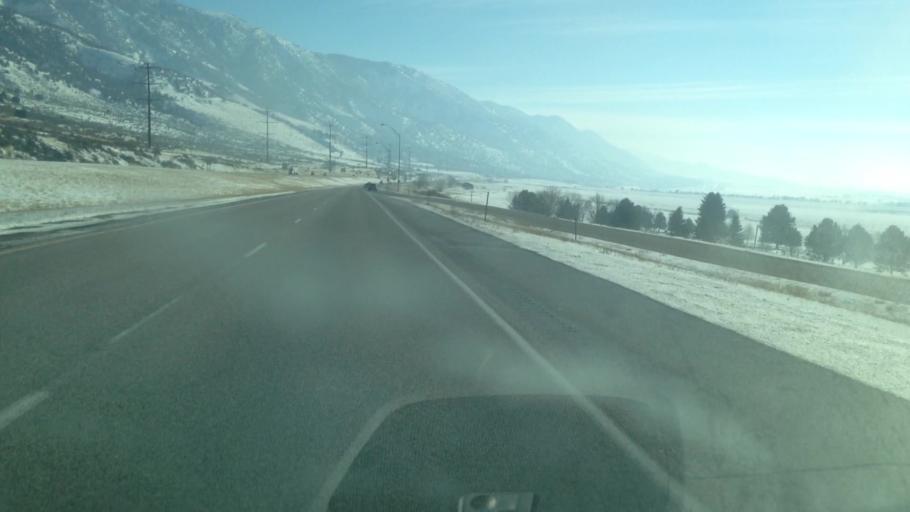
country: US
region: Idaho
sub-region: Oneida County
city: Malad City
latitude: 42.1820
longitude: -112.2321
